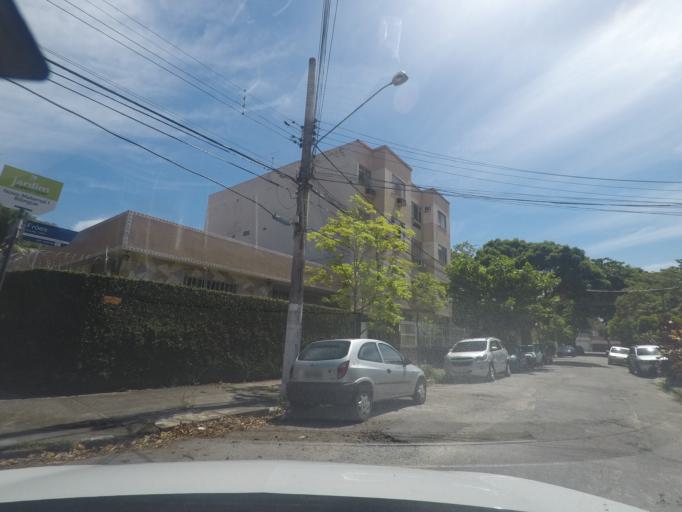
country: BR
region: Rio de Janeiro
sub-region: Niteroi
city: Niteroi
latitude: -22.9178
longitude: -43.0891
